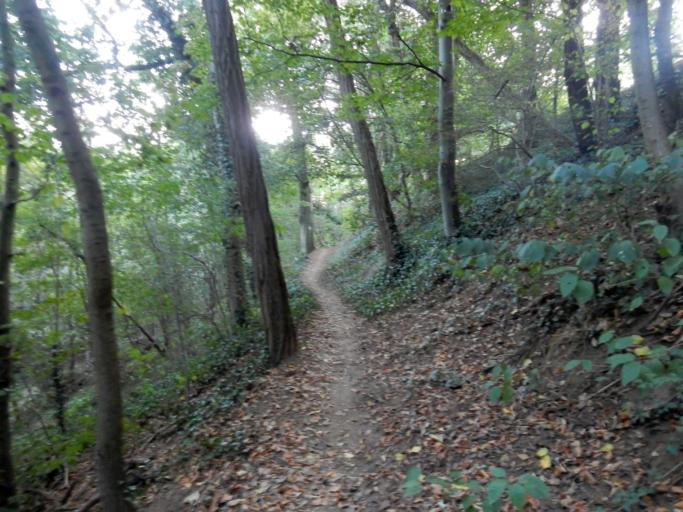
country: LU
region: Luxembourg
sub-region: Canton de Luxembourg
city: Luxembourg
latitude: 49.6015
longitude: 6.1483
